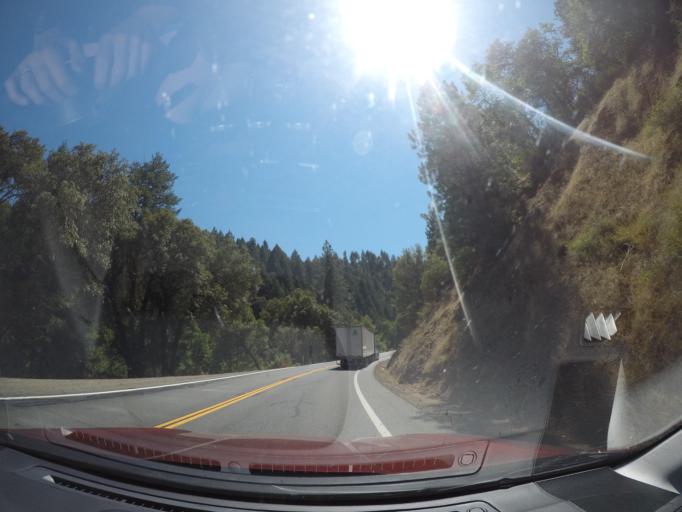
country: US
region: California
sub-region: Shasta County
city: Bella Vista
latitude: 40.7471
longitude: -122.0547
